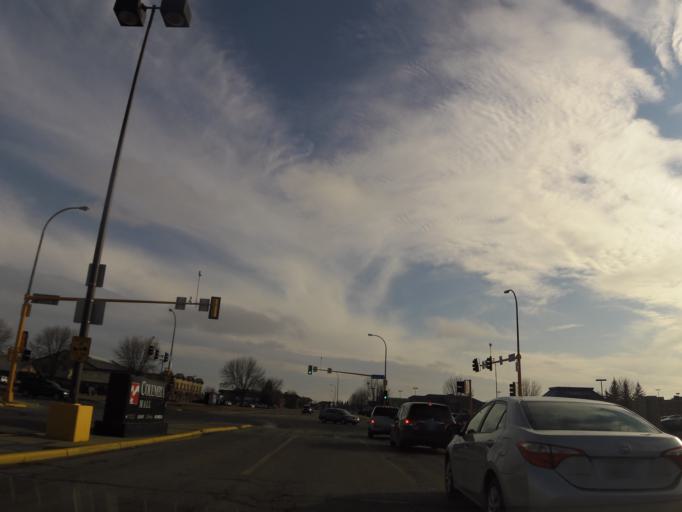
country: US
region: North Dakota
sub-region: Grand Forks County
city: Grand Forks
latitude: 47.8900
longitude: -97.0733
